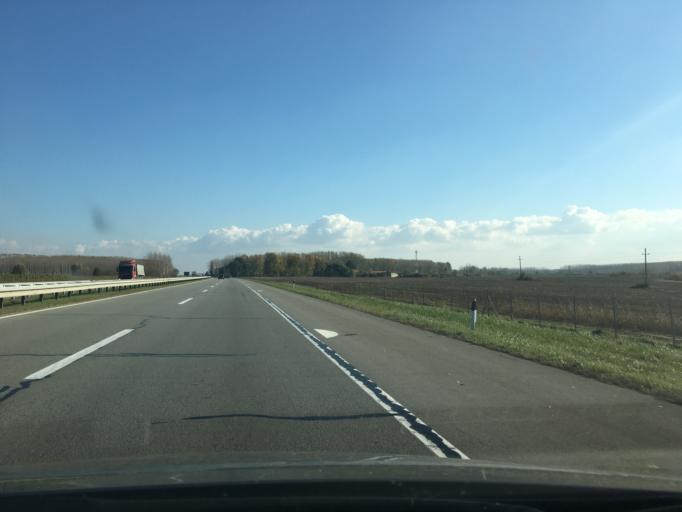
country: RS
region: Autonomna Pokrajina Vojvodina
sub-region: Juznobacki Okrug
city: Petrovaradin
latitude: 45.2807
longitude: 19.9065
